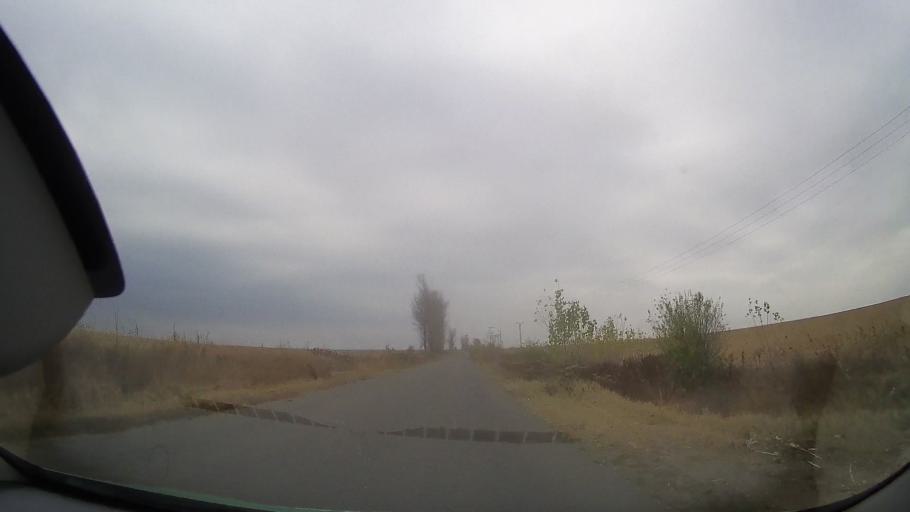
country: RO
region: Buzau
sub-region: Comuna Scutelnici
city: Scutelnici
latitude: 44.8847
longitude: 26.9546
